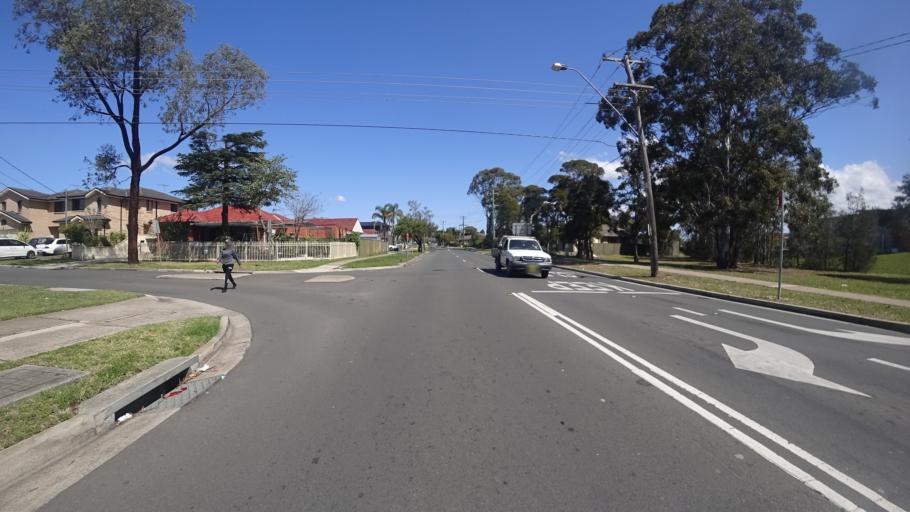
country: AU
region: New South Wales
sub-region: Liverpool
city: Miller
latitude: -33.9268
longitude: 150.8986
